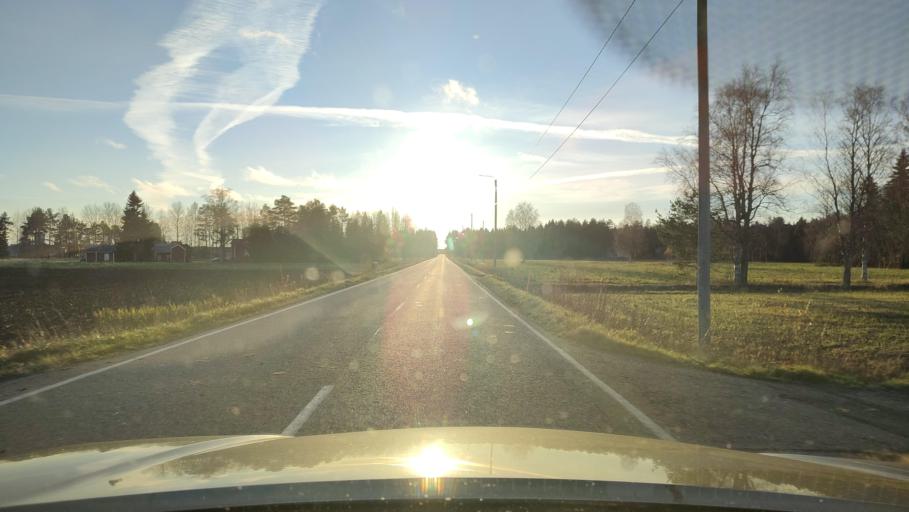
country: FI
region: Ostrobothnia
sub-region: Vaasa
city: Malax
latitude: 62.7015
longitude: 21.5856
